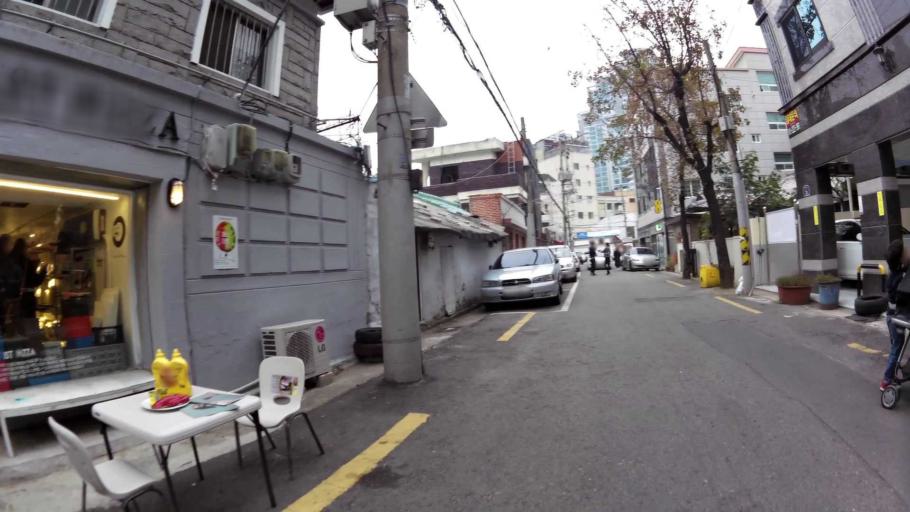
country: KR
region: Daegu
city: Daegu
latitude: 35.8609
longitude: 128.6052
